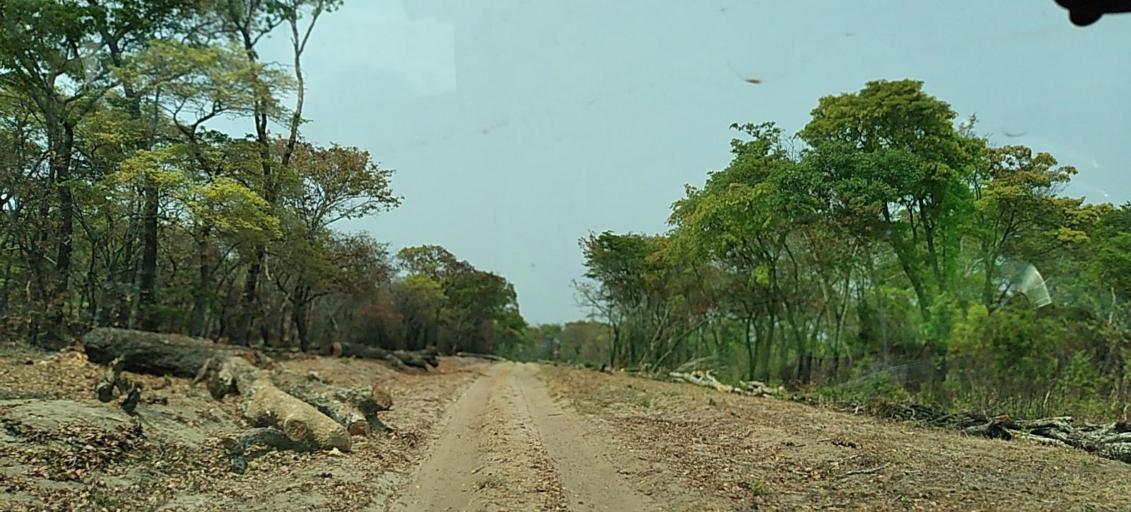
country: ZM
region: Western
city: Lukulu
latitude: -13.9567
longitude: 23.2248
